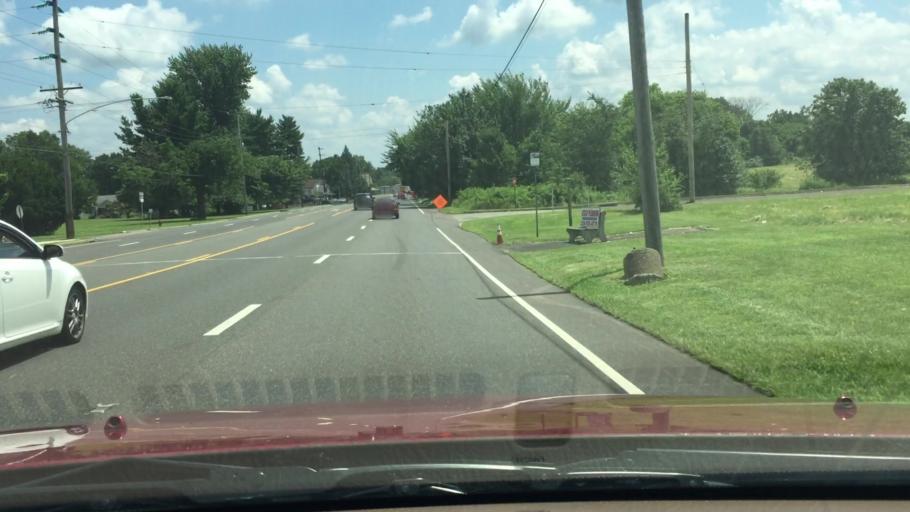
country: US
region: Pennsylvania
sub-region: Montgomery County
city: Horsham
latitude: 40.1873
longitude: -75.1344
